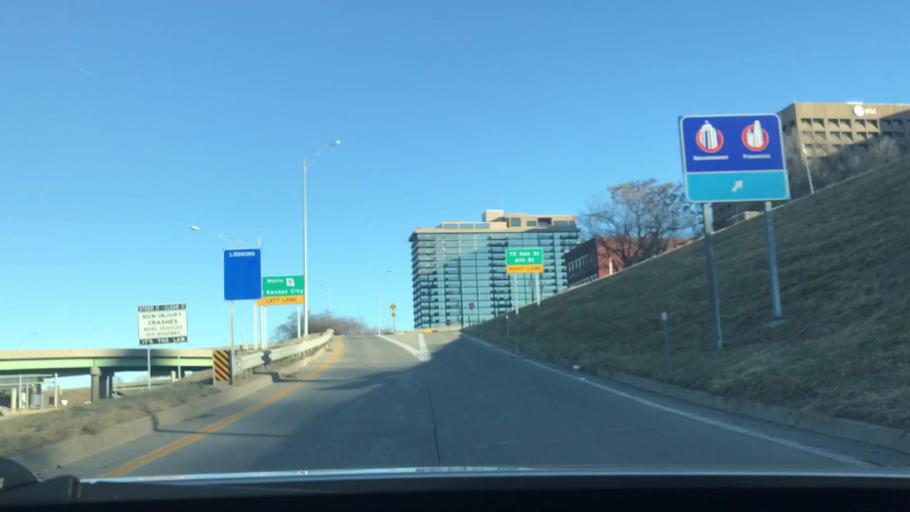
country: US
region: Missouri
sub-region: Jackson County
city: Kansas City
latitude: 39.1065
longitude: -94.5794
